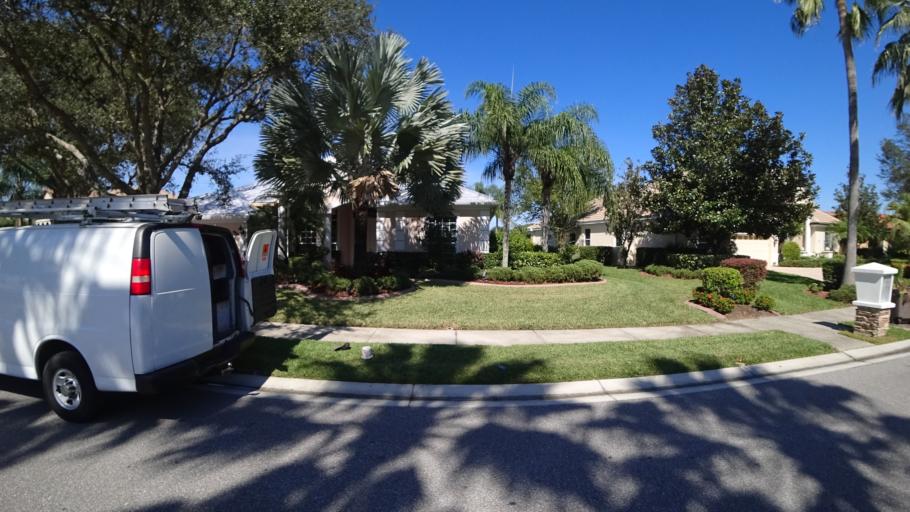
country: US
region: Florida
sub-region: Sarasota County
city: The Meadows
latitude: 27.3987
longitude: -82.4229
